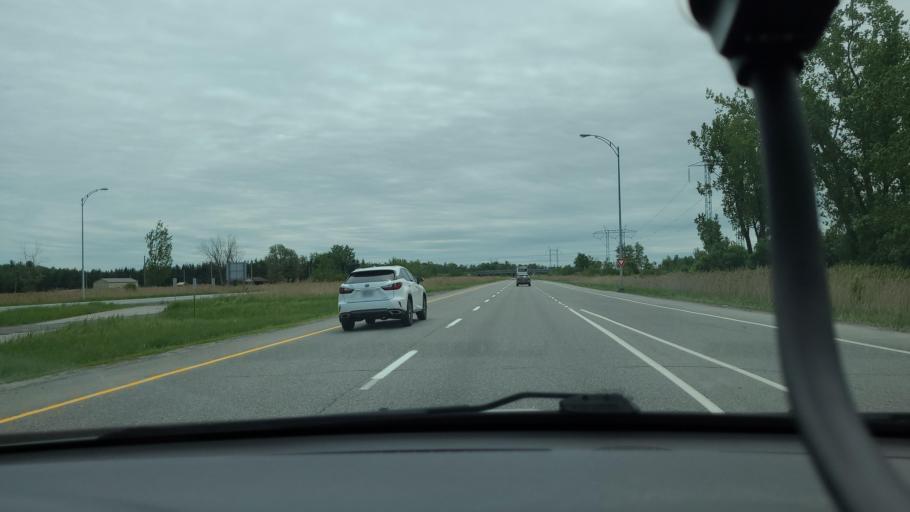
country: CA
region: Quebec
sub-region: Lanaudiere
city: Mascouche
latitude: 45.7859
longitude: -73.5775
